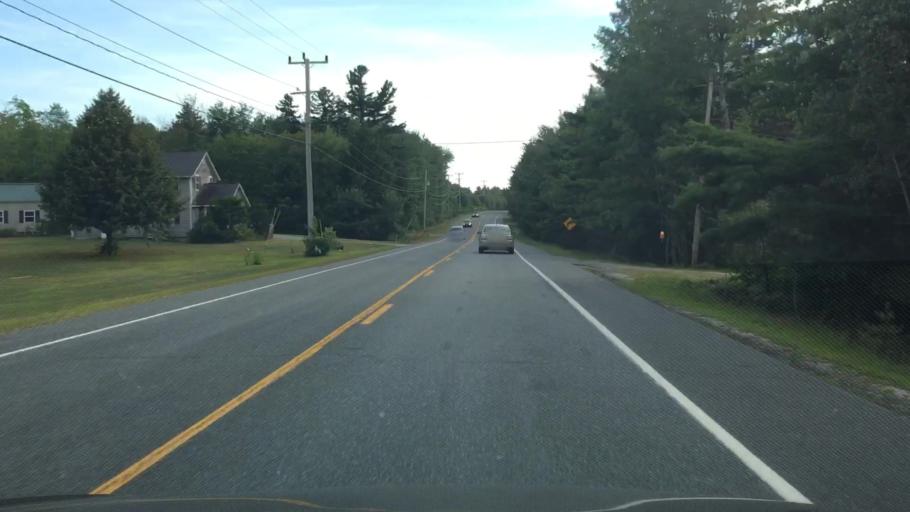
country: US
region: Maine
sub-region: Hancock County
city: Surry
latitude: 44.4461
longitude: -68.5619
